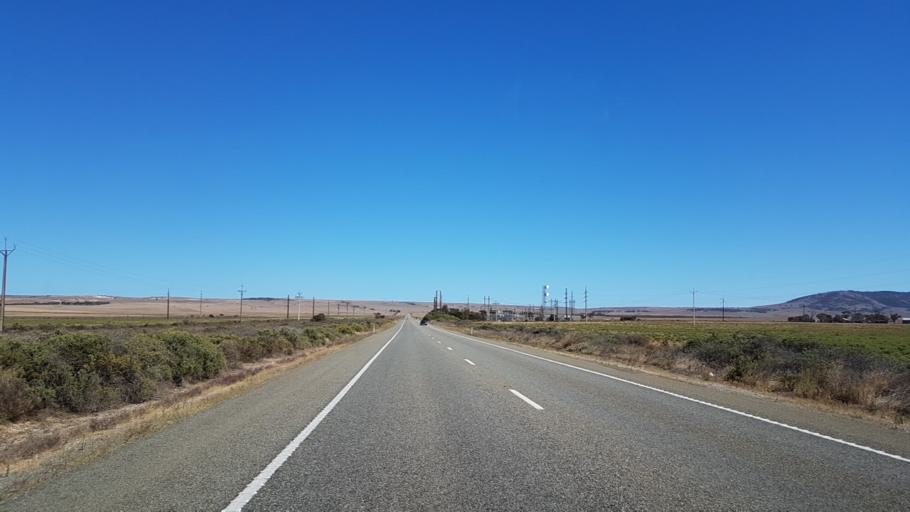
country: AU
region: South Australia
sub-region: Wakefield
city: Balaklava
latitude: -34.0914
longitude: 138.0946
